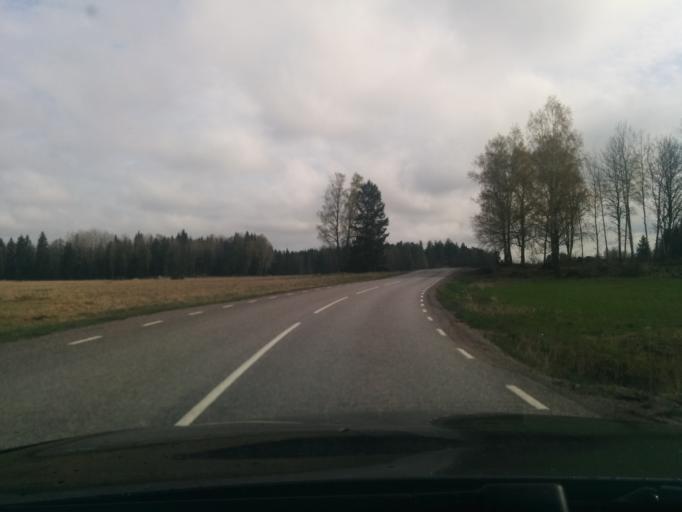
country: SE
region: Uppsala
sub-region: Tierps Kommun
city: Orbyhus
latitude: 60.1874
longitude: 17.6758
